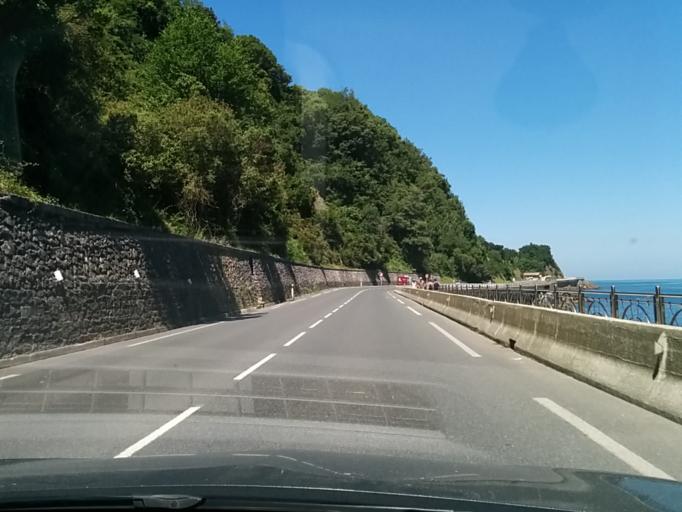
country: ES
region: Basque Country
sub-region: Provincia de Guipuzcoa
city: Getaria
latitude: 43.2926
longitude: -2.1905
